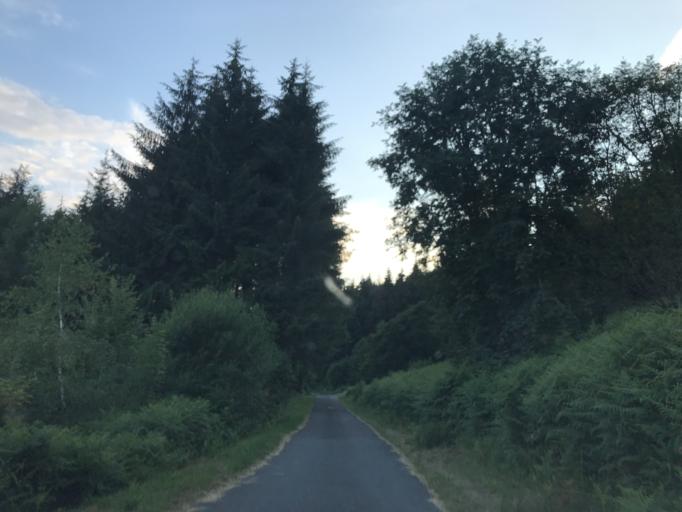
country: FR
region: Rhone-Alpes
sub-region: Departement de la Loire
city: Noiretable
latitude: 45.7982
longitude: 3.6995
